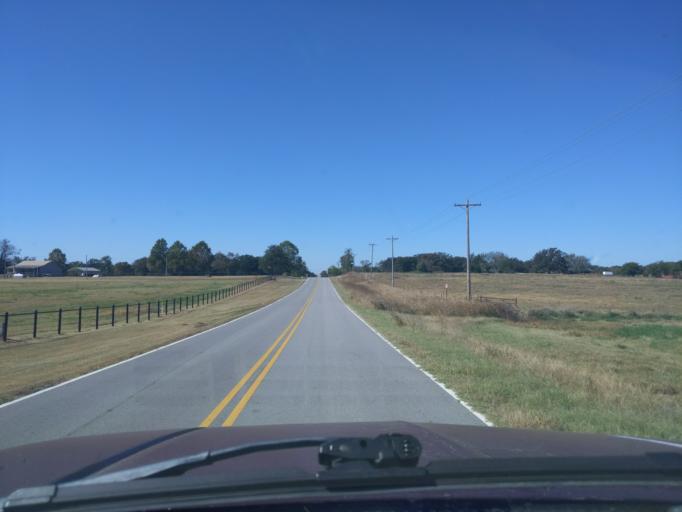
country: US
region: Oklahoma
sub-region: Creek County
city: Bristow
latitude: 35.7120
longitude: -96.4006
